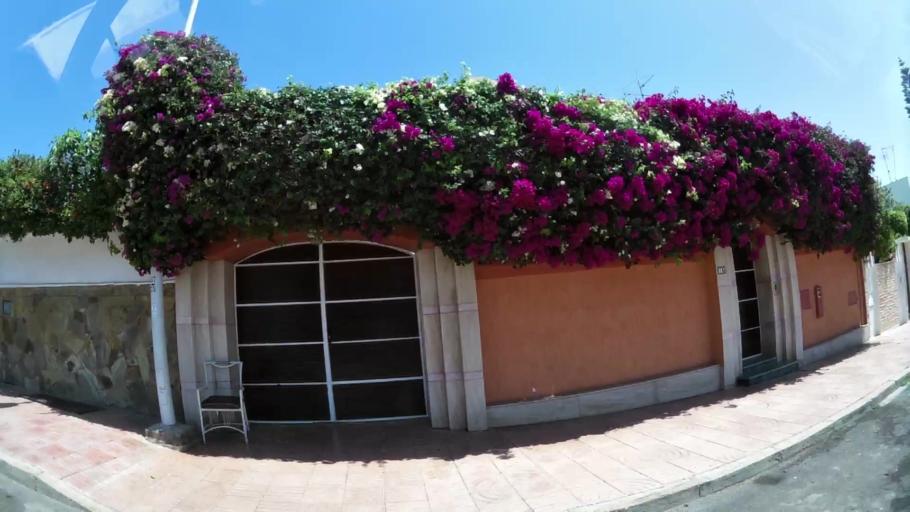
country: MA
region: Souss-Massa-Draa
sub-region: Agadir-Ida-ou-Tnan
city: Agadir
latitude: 30.4351
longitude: -9.5851
